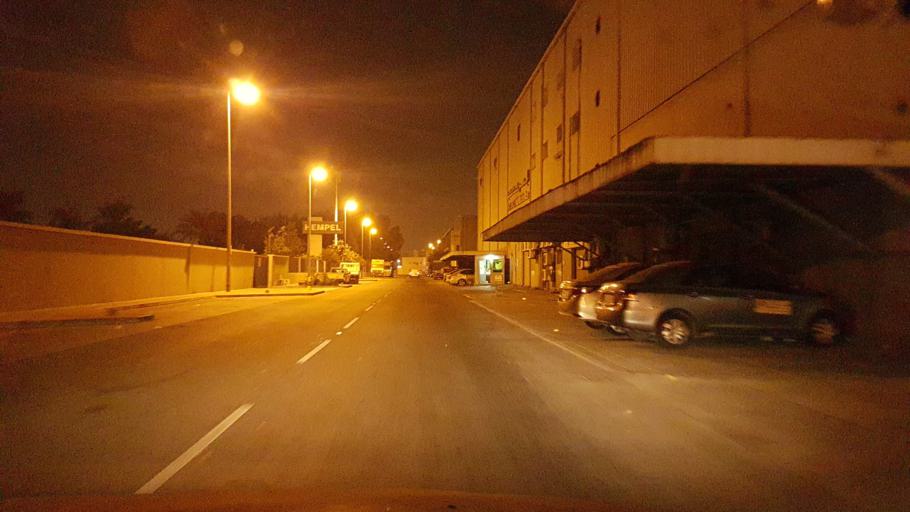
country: BH
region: Manama
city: Manama
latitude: 26.2008
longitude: 50.5996
